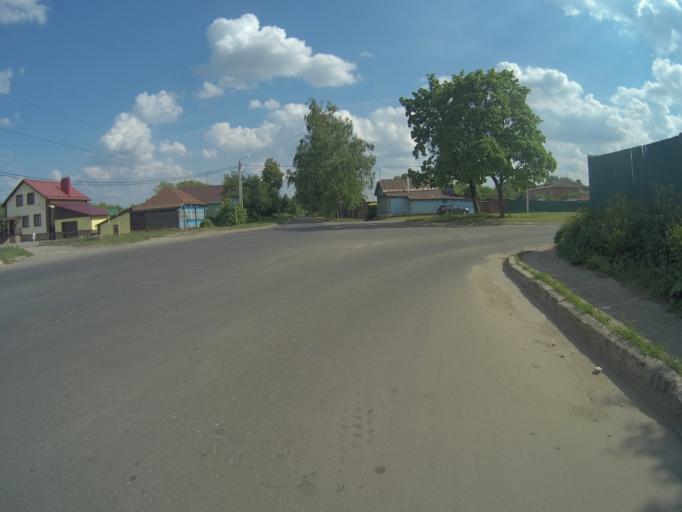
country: RU
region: Vladimir
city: Suzdal'
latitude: 56.4268
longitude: 40.4547
